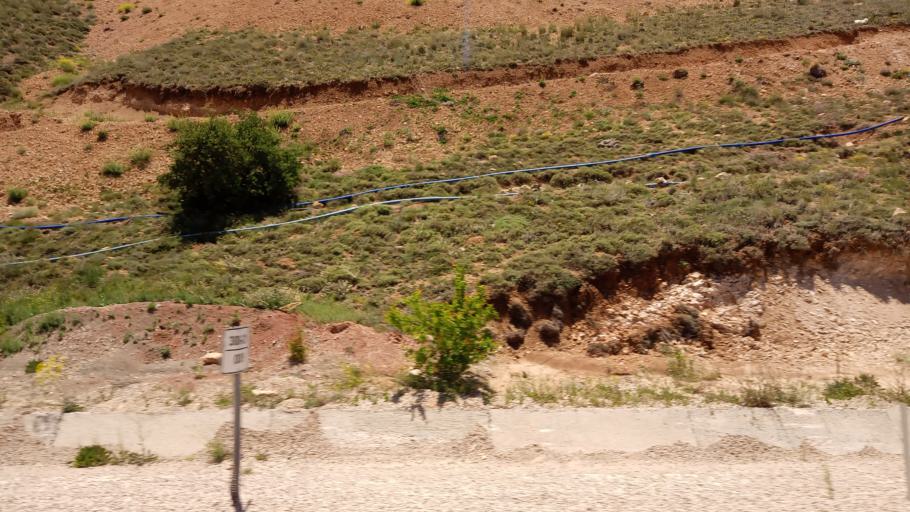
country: TR
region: Malatya
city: Darende
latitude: 38.6148
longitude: 37.4593
